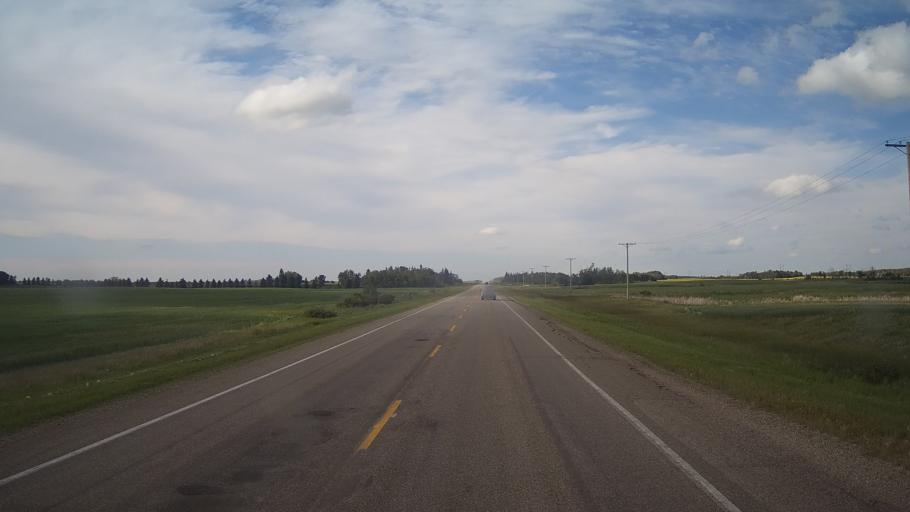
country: CA
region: Saskatchewan
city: Foam Lake
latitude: 51.5956
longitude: -103.8459
